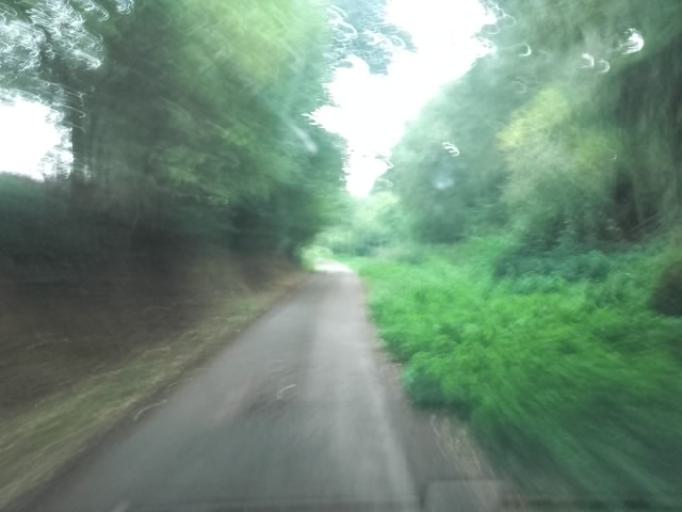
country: FR
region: Brittany
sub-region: Departement des Cotes-d'Armor
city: Pleguien
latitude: 48.6369
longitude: -2.9524
